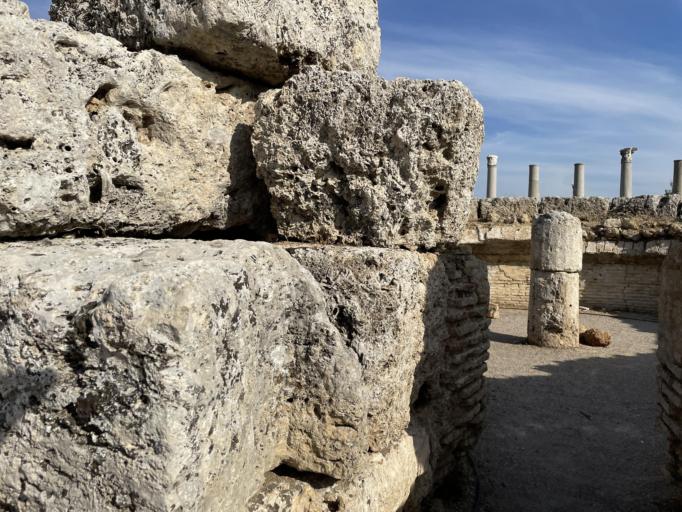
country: TR
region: Antalya
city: Aksu
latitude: 36.9614
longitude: 30.8548
